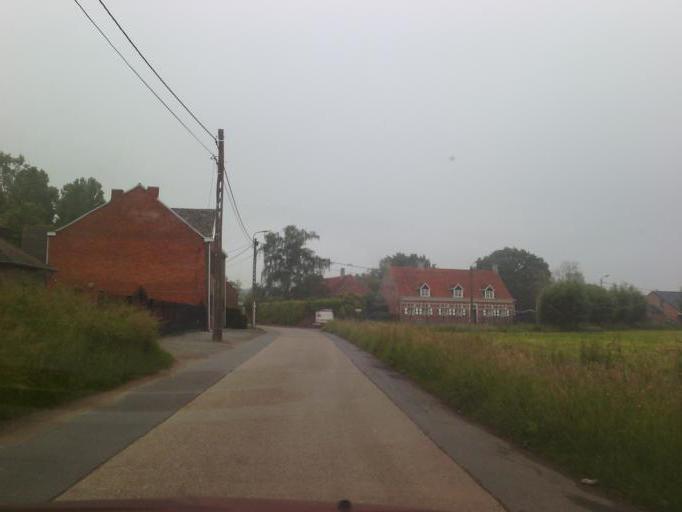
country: BE
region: Flanders
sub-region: Provincie Oost-Vlaanderen
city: Berlare
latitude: 51.0045
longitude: 4.0301
